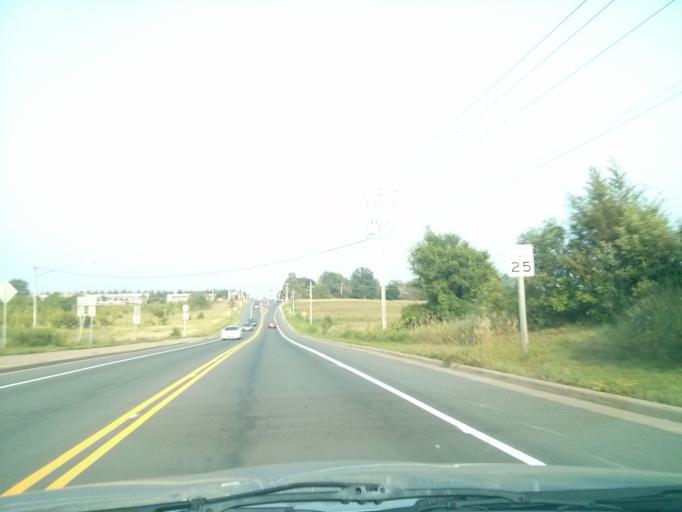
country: US
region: Wisconsin
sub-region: Saint Croix County
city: Hudson
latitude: 44.9778
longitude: -92.7257
